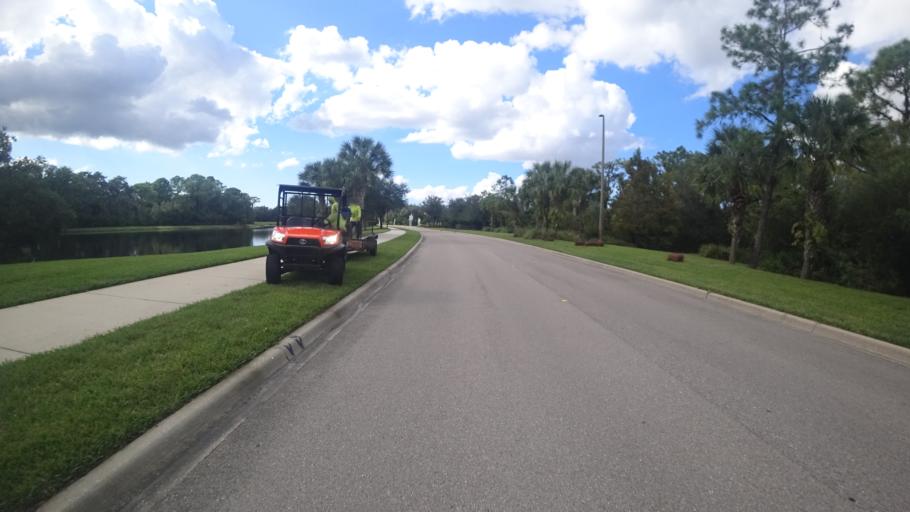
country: US
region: Florida
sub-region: Sarasota County
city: The Meadows
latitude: 27.4067
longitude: -82.4262
